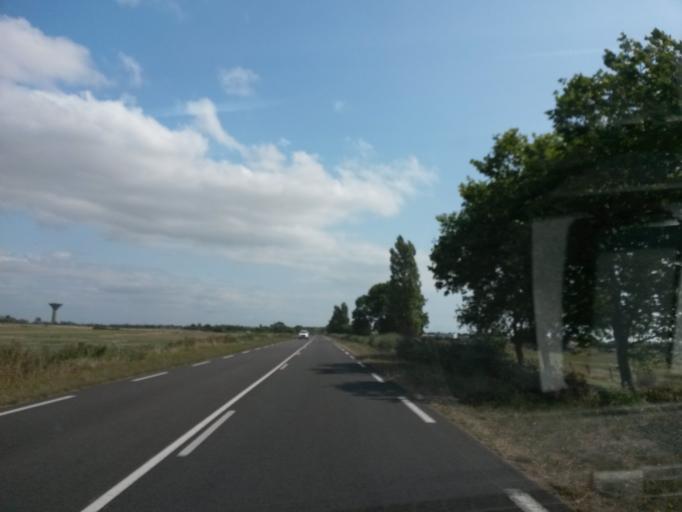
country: FR
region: Pays de la Loire
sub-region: Departement de la Vendee
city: La Tranche-sur-Mer
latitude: 46.3565
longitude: -1.4417
